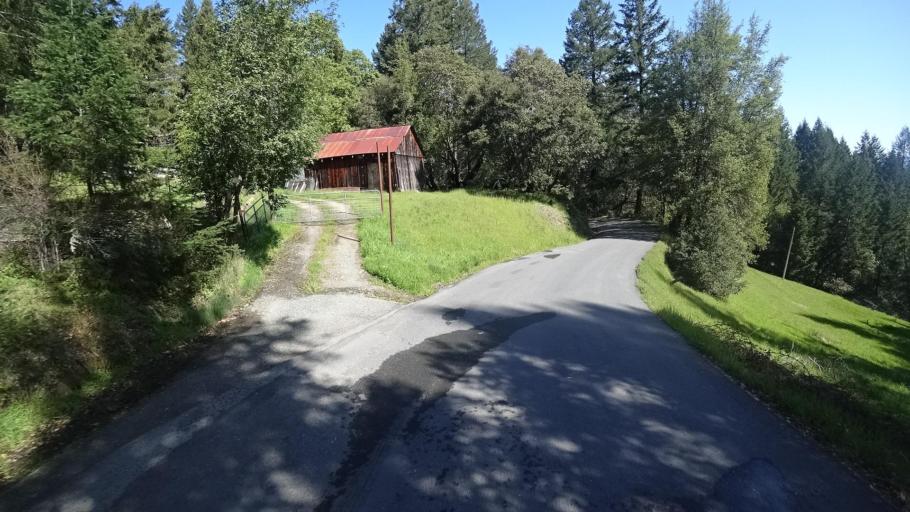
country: US
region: California
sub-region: Humboldt County
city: Redway
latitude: 40.0734
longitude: -123.6507
